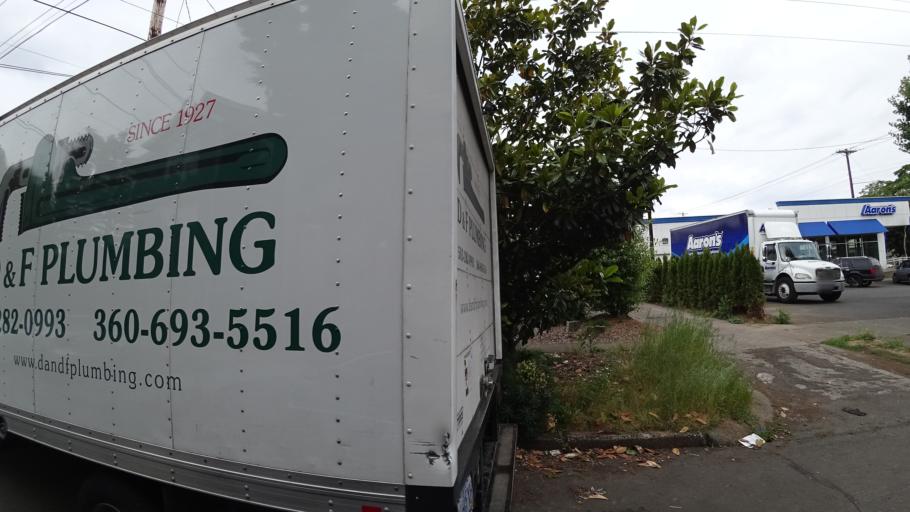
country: US
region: Oregon
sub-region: Multnomah County
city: Portland
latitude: 45.5767
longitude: -122.6833
